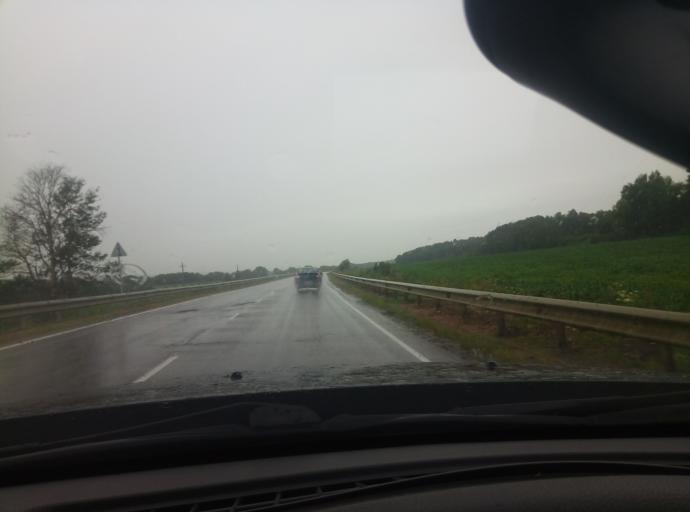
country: RU
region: Kaluga
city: Kremenki
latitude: 54.8821
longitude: 37.1096
